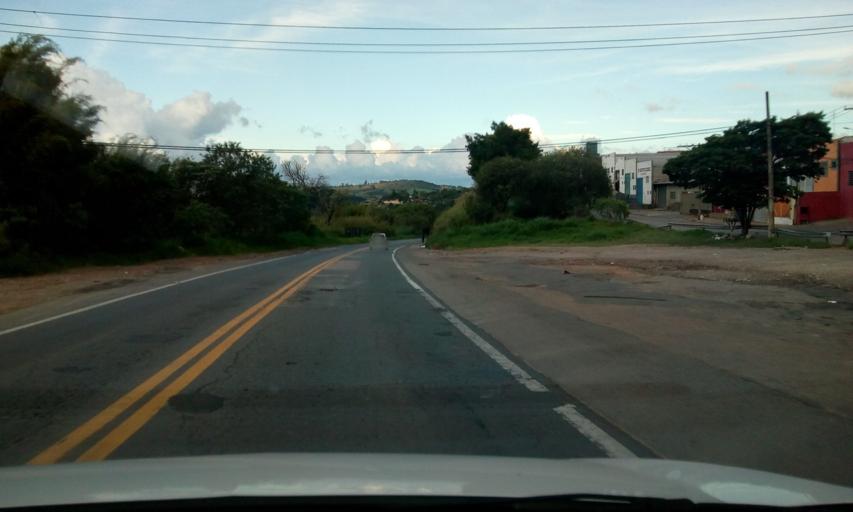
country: BR
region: Sao Paulo
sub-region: Itatiba
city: Itatiba
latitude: -23.0033
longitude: -46.8153
